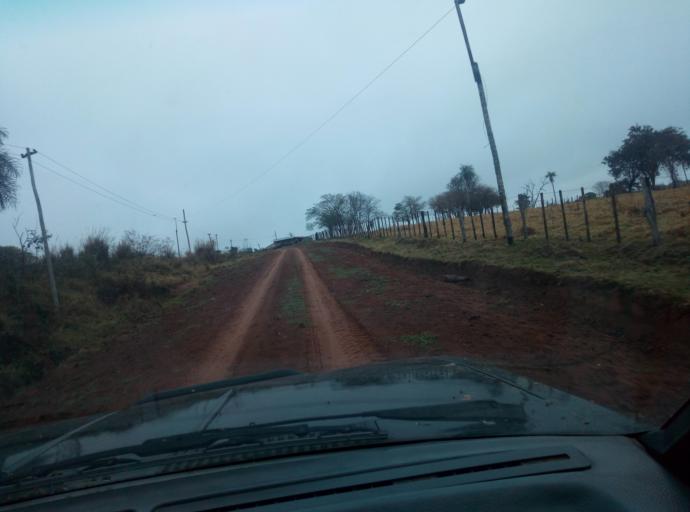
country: PY
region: Caaguazu
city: Carayao
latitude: -25.1934
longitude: -56.3245
